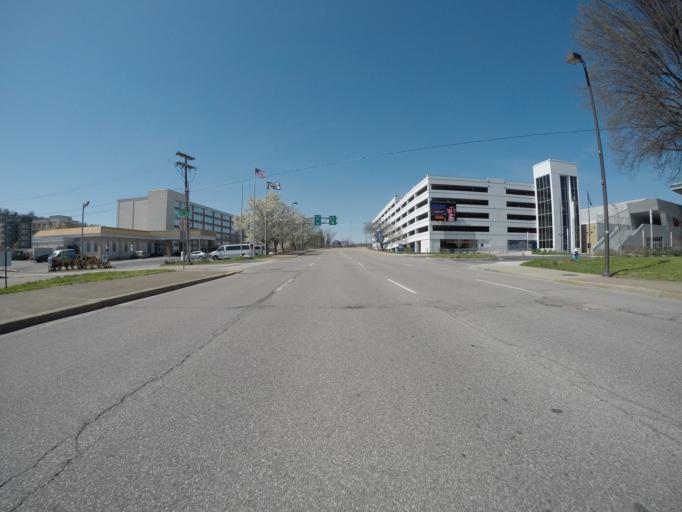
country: US
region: West Virginia
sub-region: Kanawha County
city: Charleston
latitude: 38.3550
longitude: -81.6414
